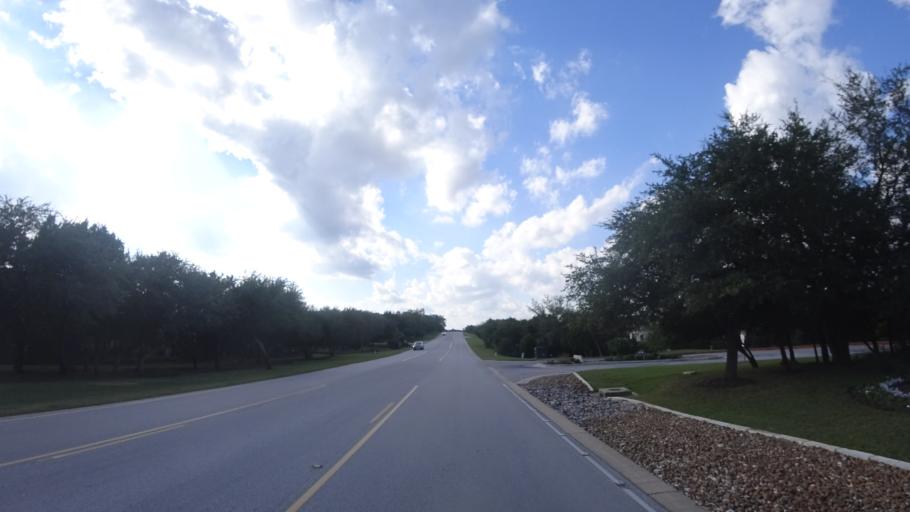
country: US
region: Texas
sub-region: Travis County
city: Barton Creek
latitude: 30.2893
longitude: -97.8677
